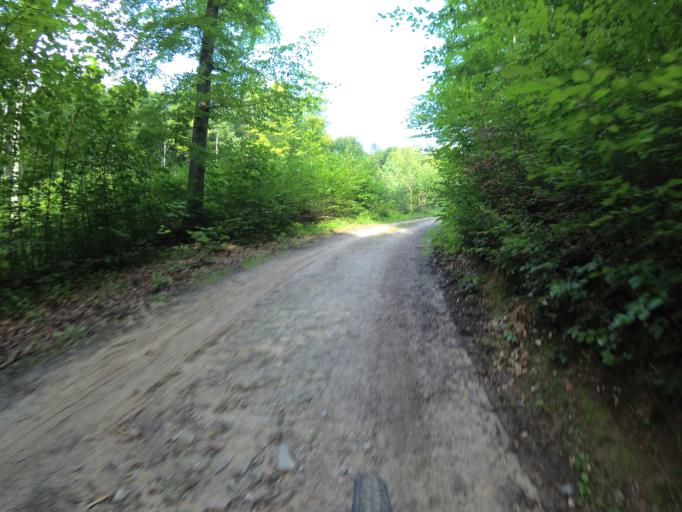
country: PL
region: Pomeranian Voivodeship
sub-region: Gdynia
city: Wielki Kack
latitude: 54.4927
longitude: 18.4752
